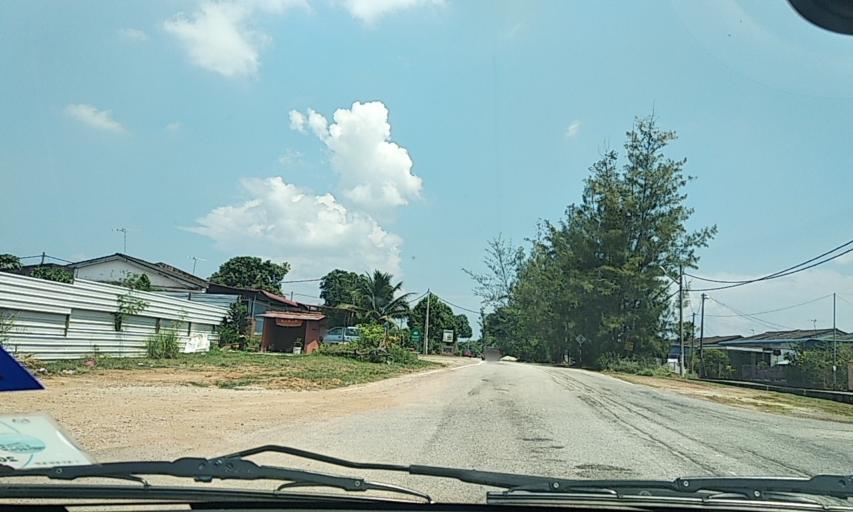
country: MY
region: Kedah
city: Sungai Petani
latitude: 5.6341
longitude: 100.4668
